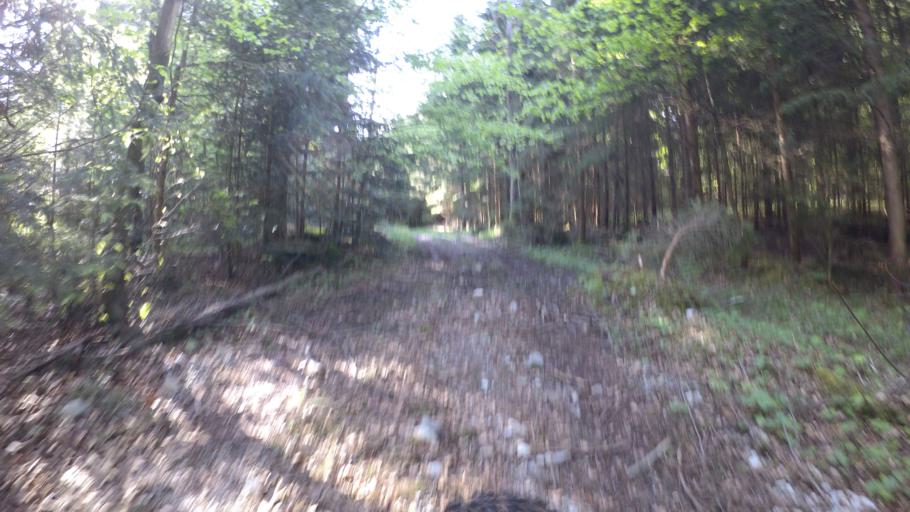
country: DE
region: Bavaria
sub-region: Upper Bavaria
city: Grabenstatt
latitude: 47.8501
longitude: 12.5719
